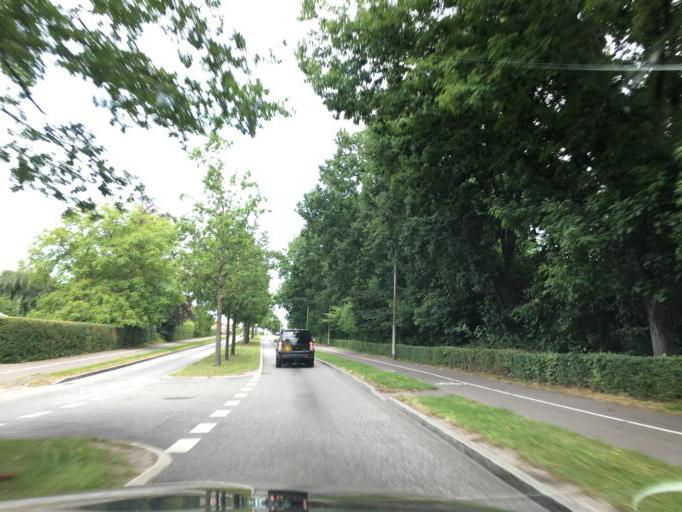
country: DK
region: Capital Region
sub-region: Horsholm Kommune
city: Horsholm
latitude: 55.8955
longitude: 12.4999
